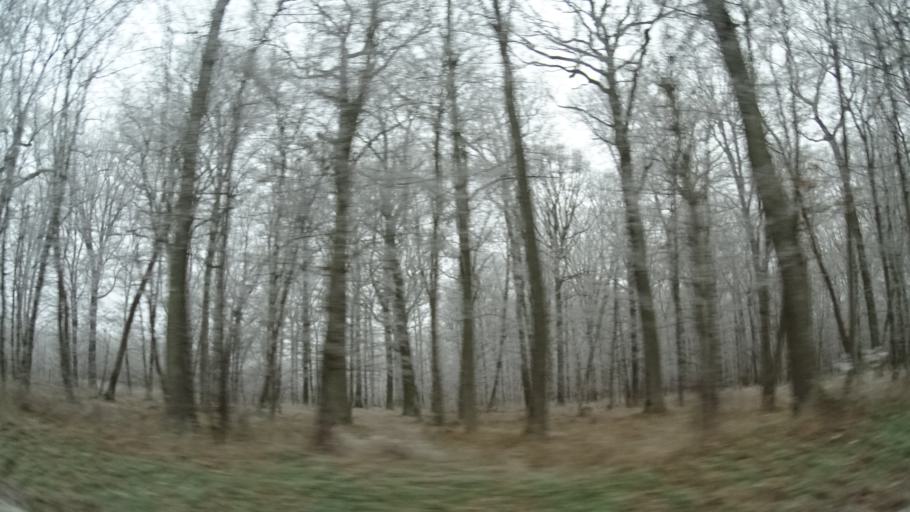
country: DE
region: Bavaria
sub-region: Regierungsbezirk Unterfranken
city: Wonfurt
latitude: 50.0194
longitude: 10.4905
